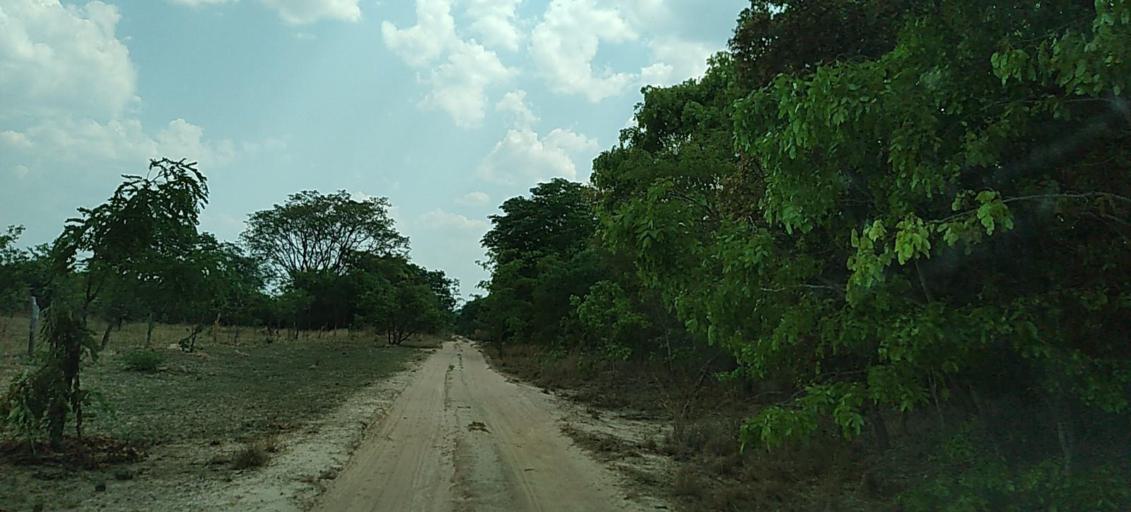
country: ZM
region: Copperbelt
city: Mpongwe
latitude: -13.8567
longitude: 27.9290
